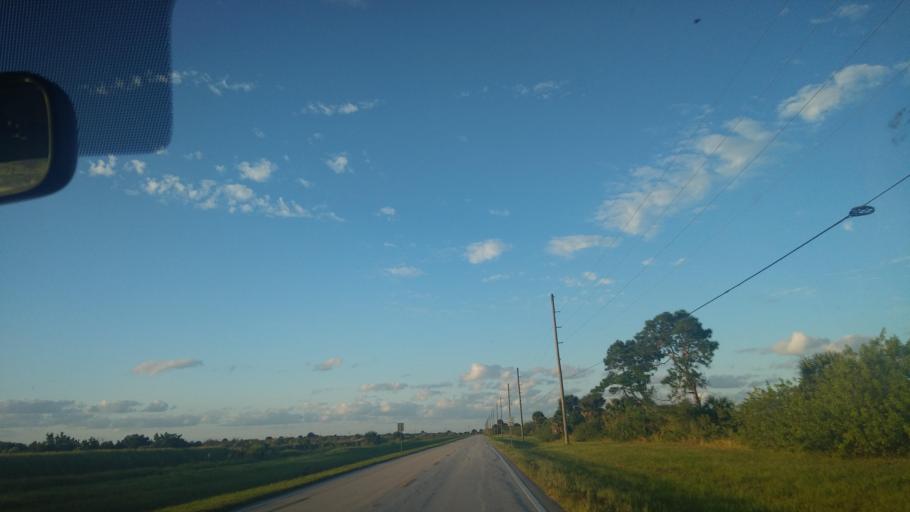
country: US
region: Florida
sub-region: Indian River County
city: Fellsmere
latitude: 27.7304
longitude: -80.6424
